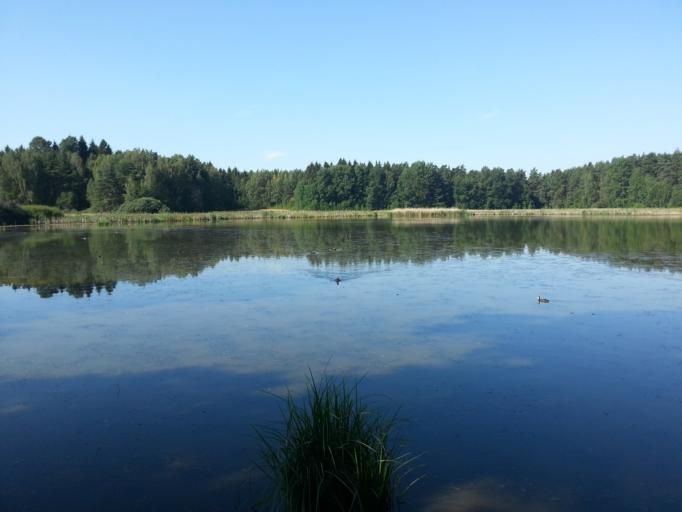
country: SE
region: OEstergoetland
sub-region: Norrkopings Kommun
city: Norrkoping
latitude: 58.5654
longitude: 16.2001
